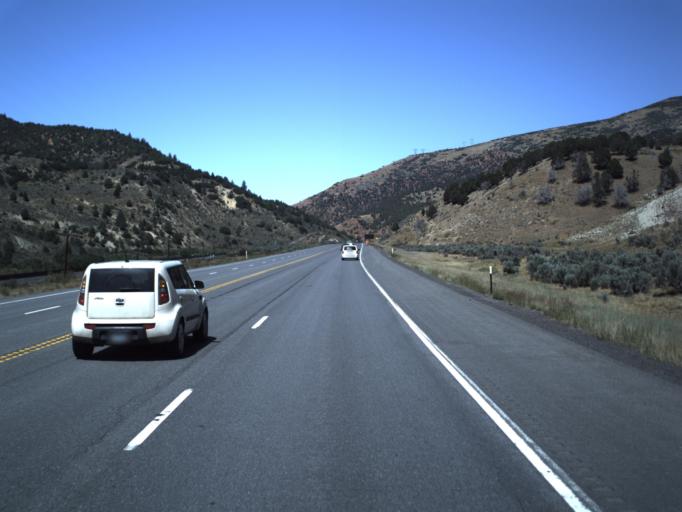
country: US
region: Utah
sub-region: Utah County
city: Mapleton
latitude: 39.9791
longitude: -111.3511
